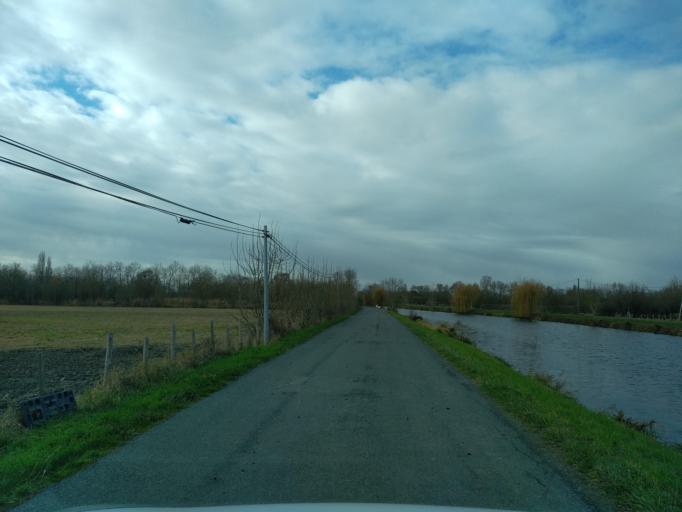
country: FR
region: Pays de la Loire
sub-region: Departement de la Vendee
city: Maillezais
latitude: 46.3183
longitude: -0.7809
